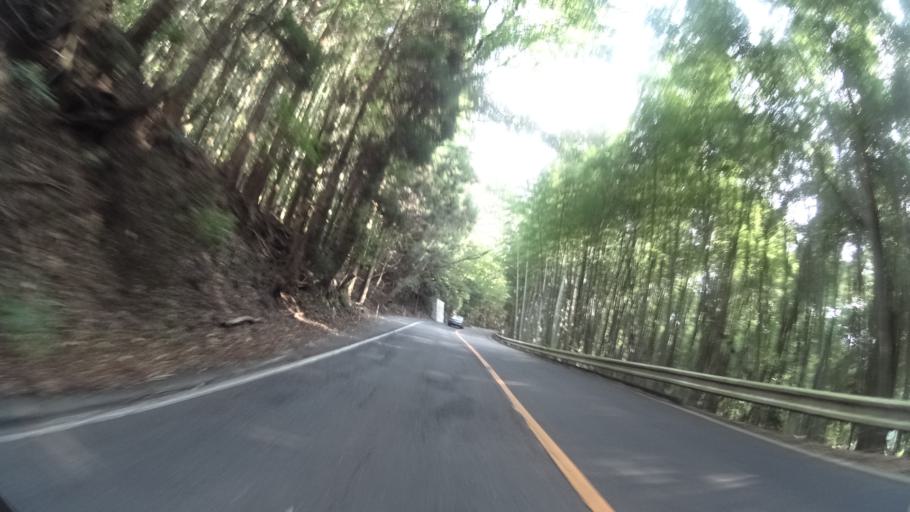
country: JP
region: Oita
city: Beppu
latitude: 33.2678
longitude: 131.3698
